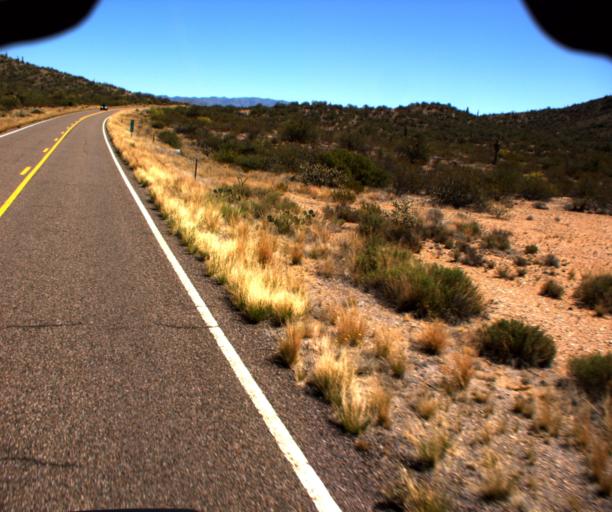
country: US
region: Arizona
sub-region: Yavapai County
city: Congress
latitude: 34.1032
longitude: -112.9957
